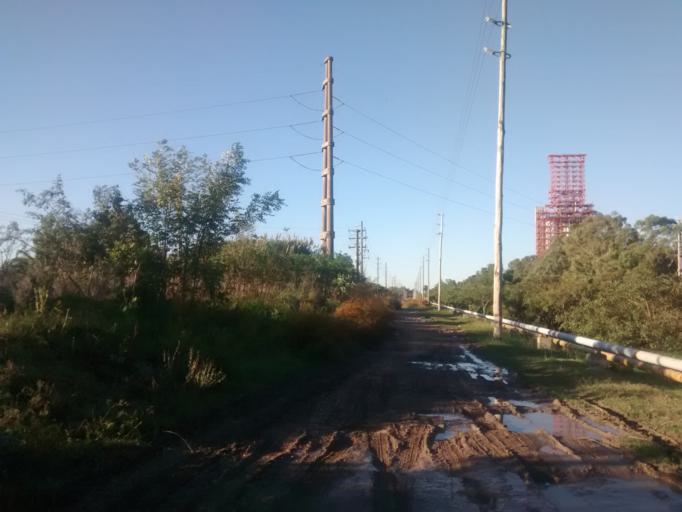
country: AR
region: Buenos Aires
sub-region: Partido de Ensenada
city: Ensenada
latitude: -34.8944
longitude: -57.9286
